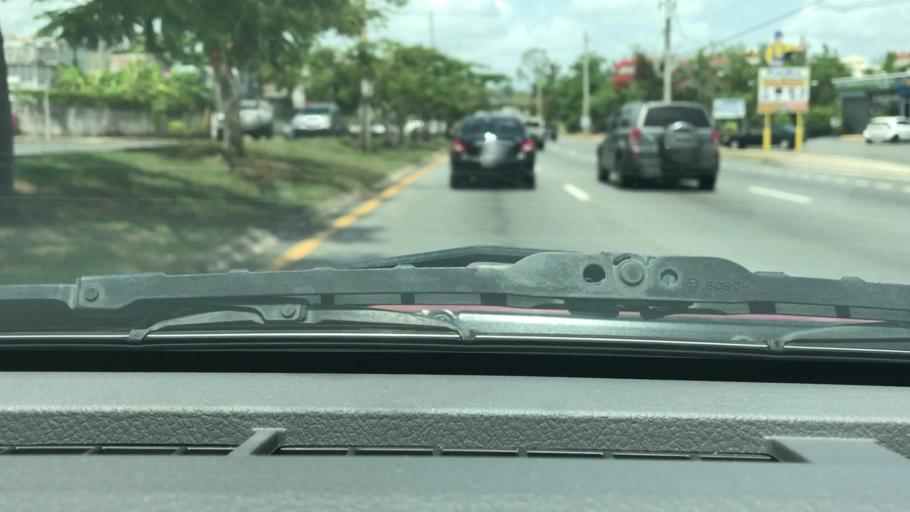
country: PR
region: Bayamon
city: Bayamon
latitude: 18.3650
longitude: -66.1771
